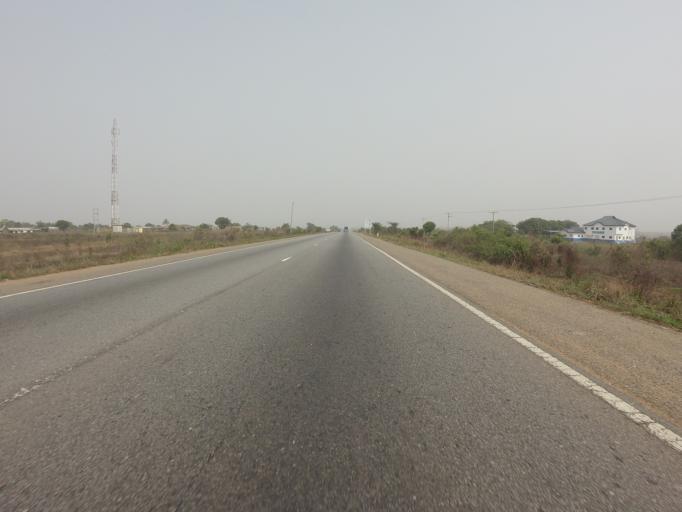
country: GH
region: Greater Accra
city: Tema
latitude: 5.8668
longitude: 0.2967
